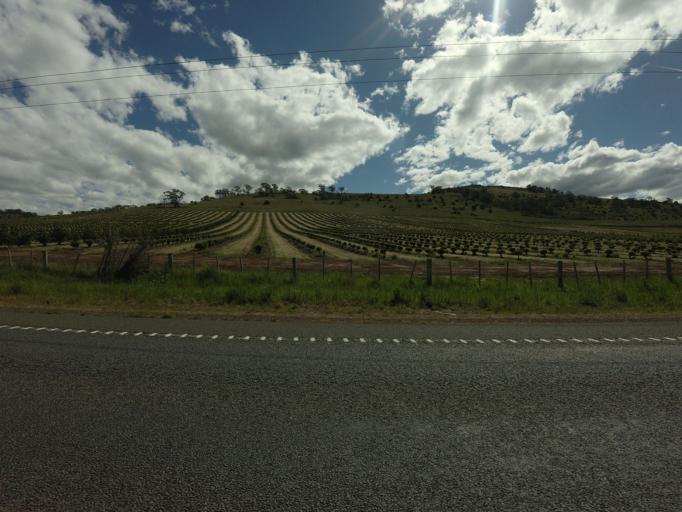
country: AU
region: Tasmania
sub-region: Northern Midlands
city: Evandale
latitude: -42.0553
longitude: 147.4824
